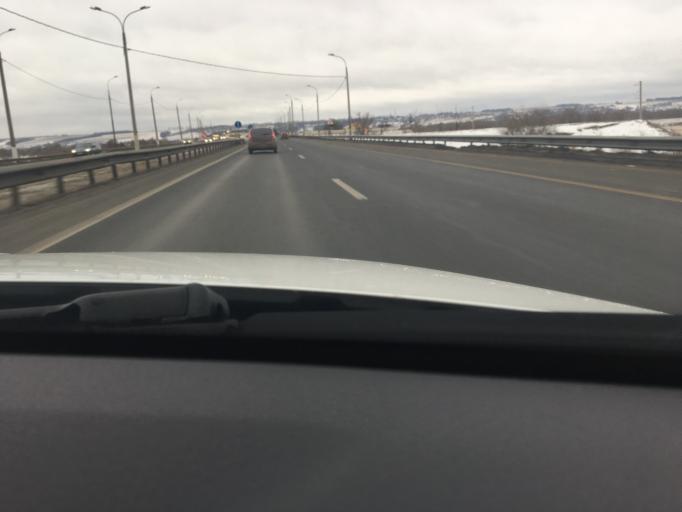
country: RU
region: Moskovskaya
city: Danki
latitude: 54.8767
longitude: 37.5074
